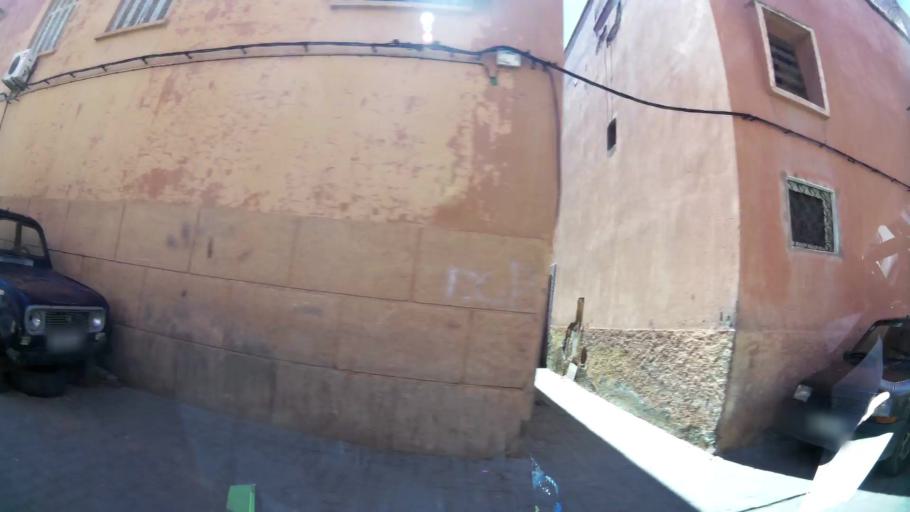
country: MA
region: Marrakech-Tensift-Al Haouz
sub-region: Marrakech
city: Marrakesh
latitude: 31.6297
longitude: -8.0426
